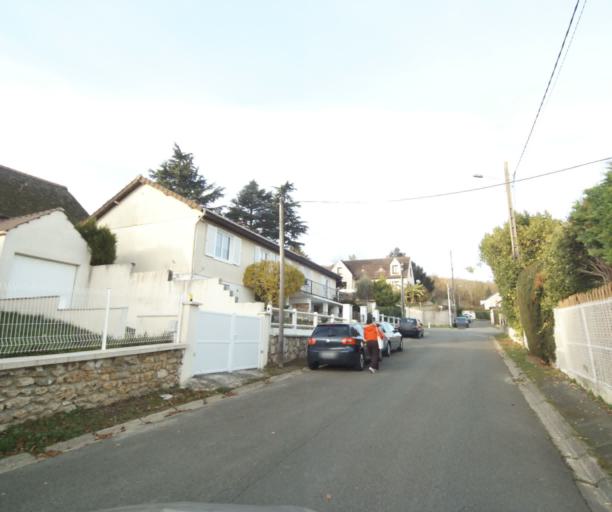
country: FR
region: Ile-de-France
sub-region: Departement des Yvelines
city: Triel-sur-Seine
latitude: 48.9895
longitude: 2.0032
